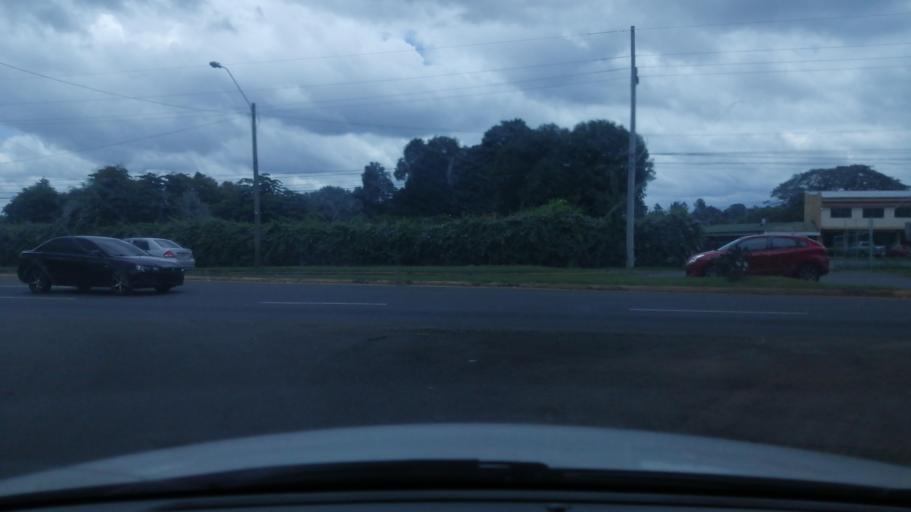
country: PA
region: Chiriqui
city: David
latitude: 8.4448
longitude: -82.4301
